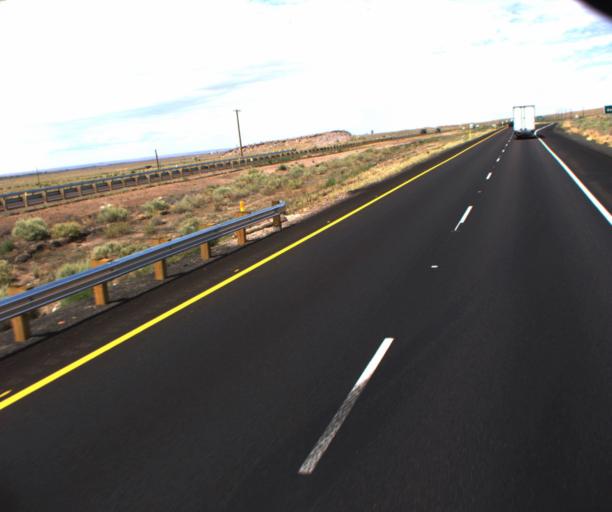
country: US
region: Arizona
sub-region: Navajo County
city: Holbrook
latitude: 34.9923
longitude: -109.9540
